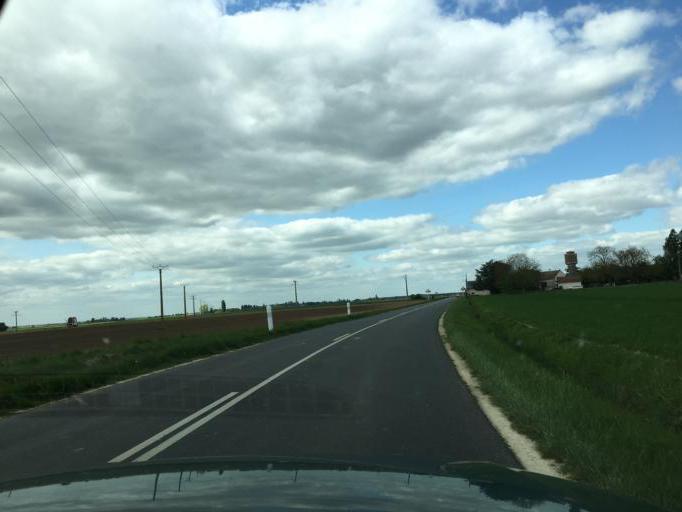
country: FR
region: Centre
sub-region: Departement du Loir-et-Cher
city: Mer
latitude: 47.8114
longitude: 1.4310
